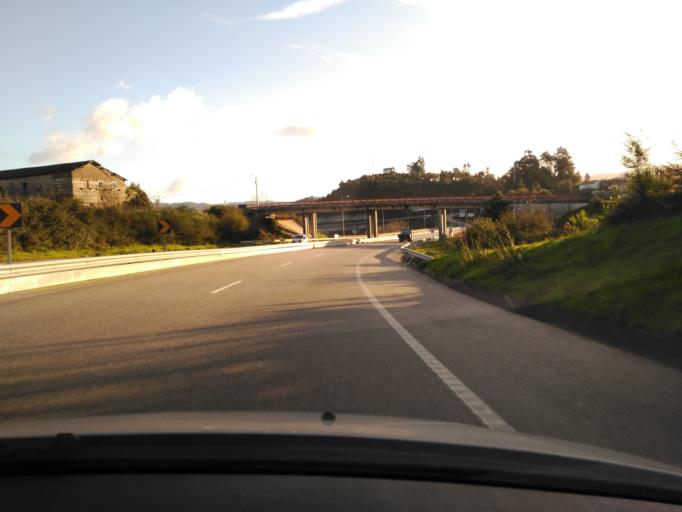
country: PT
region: Braga
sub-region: Fafe
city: Aroes
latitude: 41.4553
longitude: -8.1939
